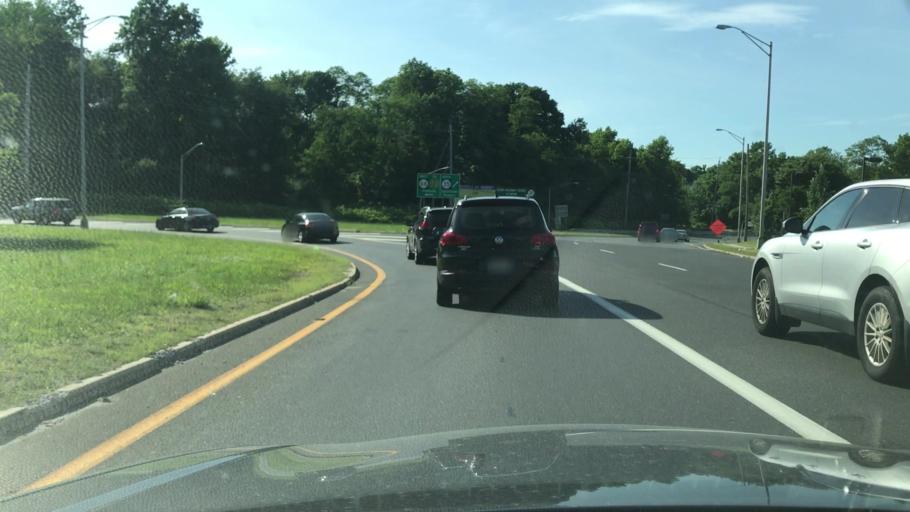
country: US
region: New Jersey
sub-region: Monmouth County
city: Wanamassa
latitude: 40.2268
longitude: -74.0383
